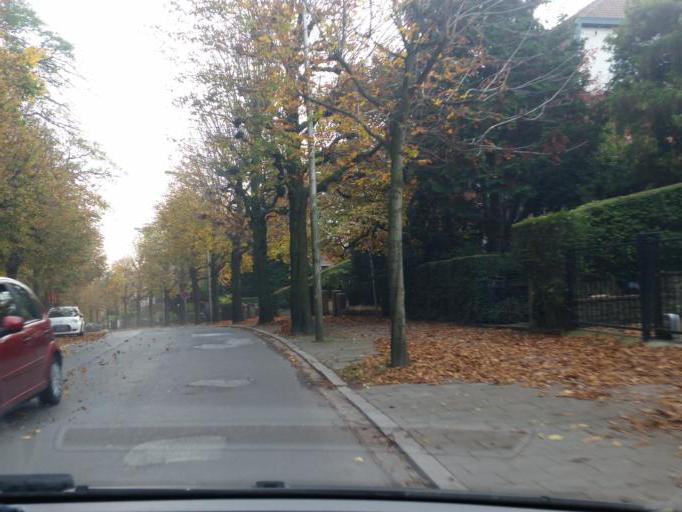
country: BE
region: Flanders
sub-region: Provincie Vlaams-Brabant
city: Dilbeek
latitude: 50.8324
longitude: 4.2949
